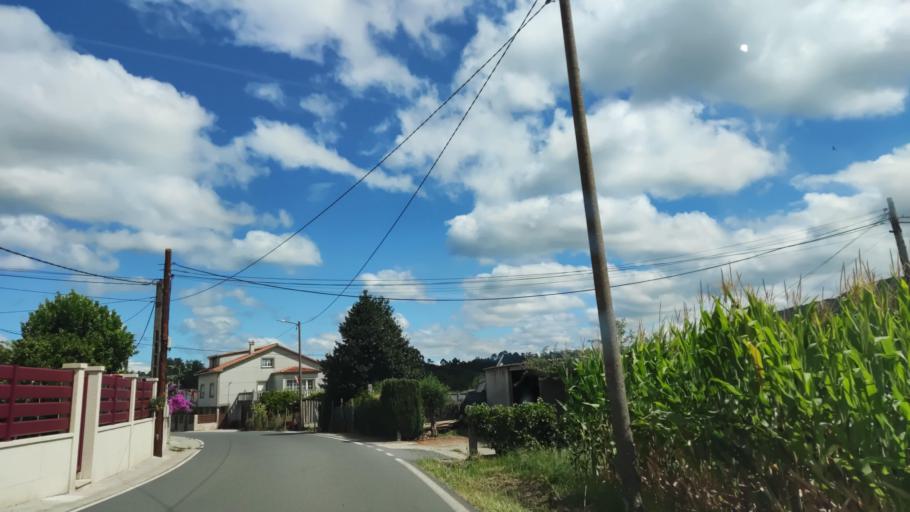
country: ES
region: Galicia
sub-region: Provincia da Coruna
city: Rois
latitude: 42.7784
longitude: -8.6696
